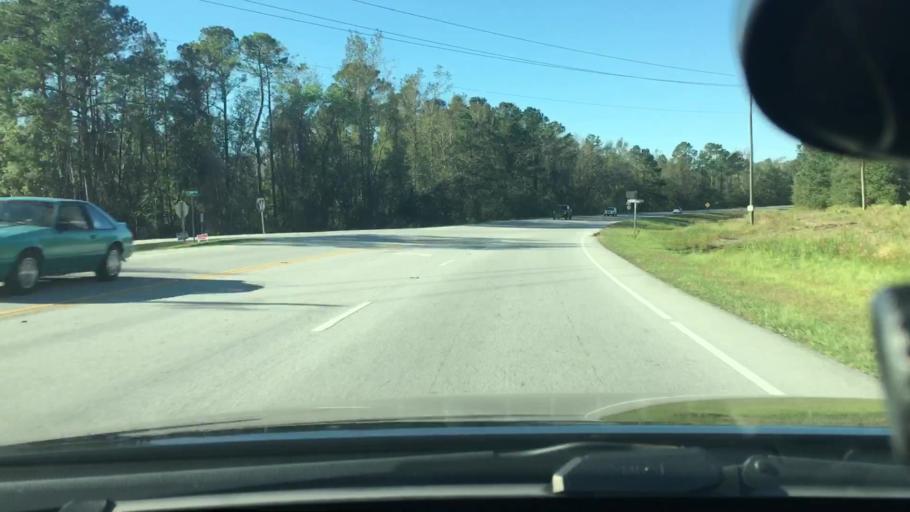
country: US
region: North Carolina
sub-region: Craven County
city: Trent Woods
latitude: 35.1739
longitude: -77.1306
